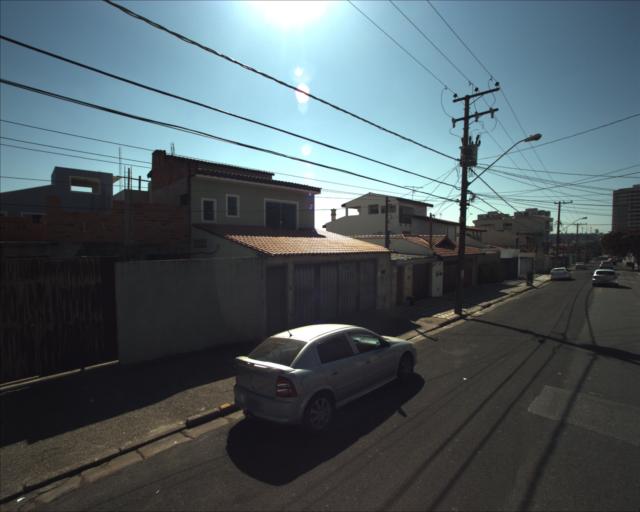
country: BR
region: Sao Paulo
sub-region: Sorocaba
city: Sorocaba
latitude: -23.4948
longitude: -47.4389
